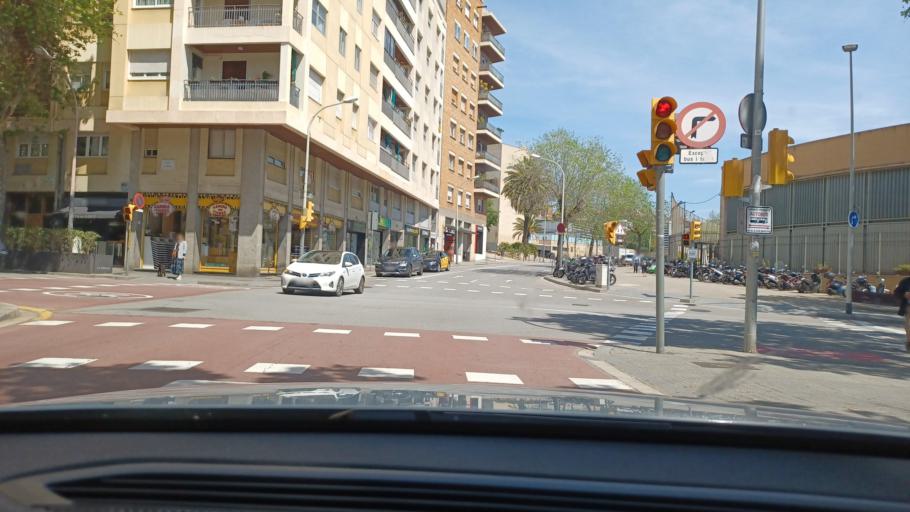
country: ES
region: Catalonia
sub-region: Provincia de Barcelona
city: les Corts
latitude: 41.3955
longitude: 2.1255
